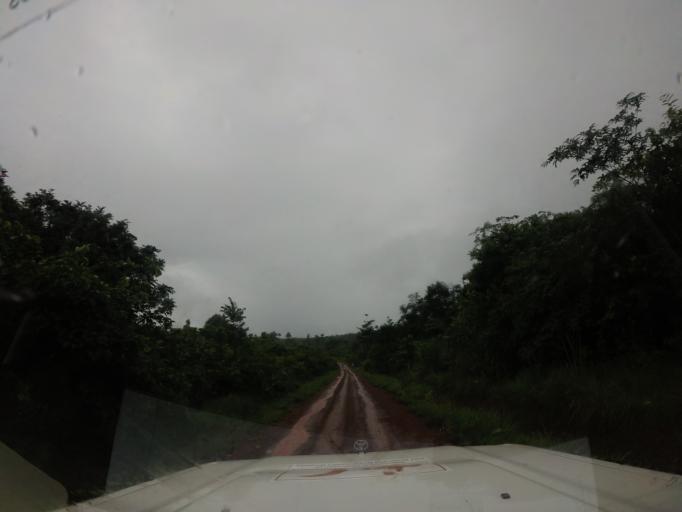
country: SL
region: Eastern Province
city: Kenema
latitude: 7.7385
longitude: -11.1910
